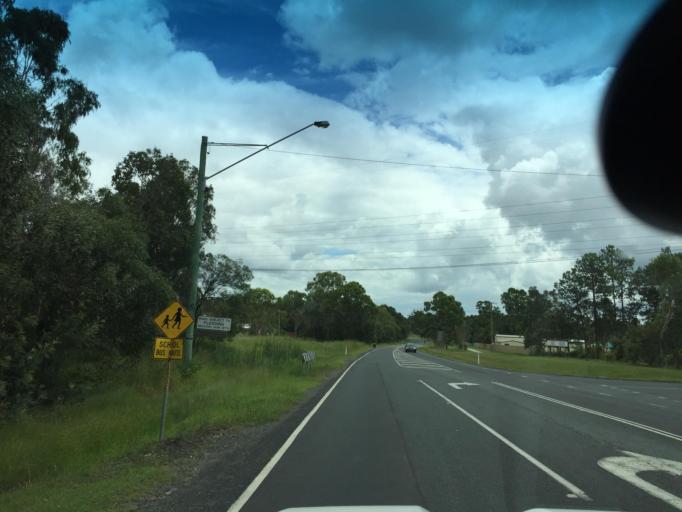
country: AU
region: Queensland
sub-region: Moreton Bay
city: Caboolture
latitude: -27.0537
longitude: 152.9390
